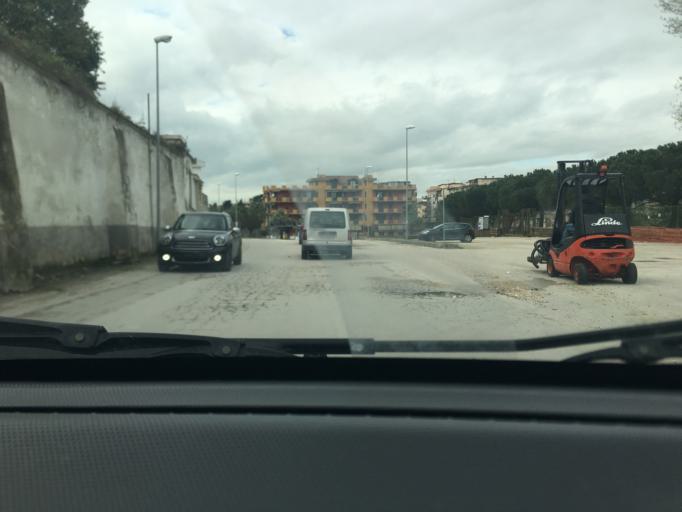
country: IT
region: Campania
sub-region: Provincia di Napoli
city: Mugnano di Napoli
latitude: 40.8957
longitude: 14.1992
